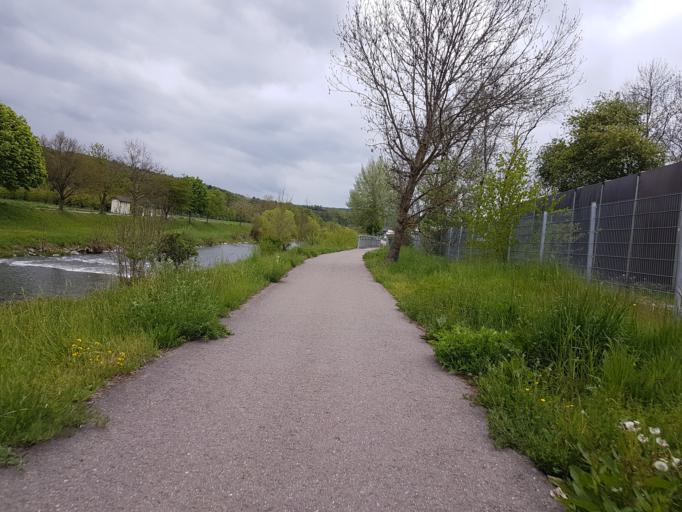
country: DE
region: Baden-Wuerttemberg
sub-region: Freiburg Region
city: Wutoschingen
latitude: 47.6432
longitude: 8.3499
